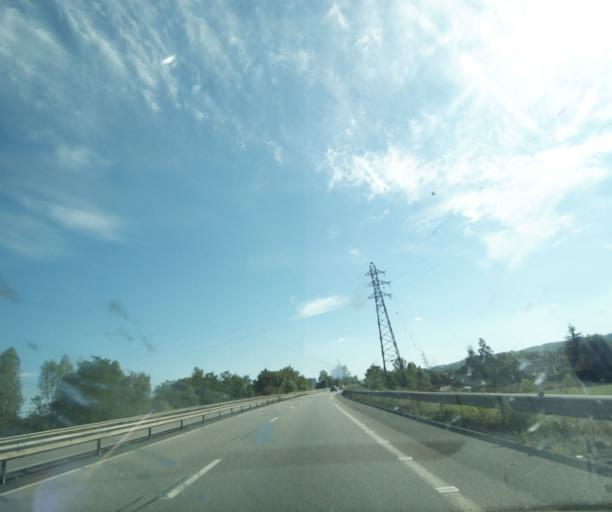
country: FR
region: Limousin
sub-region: Departement de la Correze
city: Saint-Pantaleon-de-Larche
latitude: 45.1576
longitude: 1.4820
